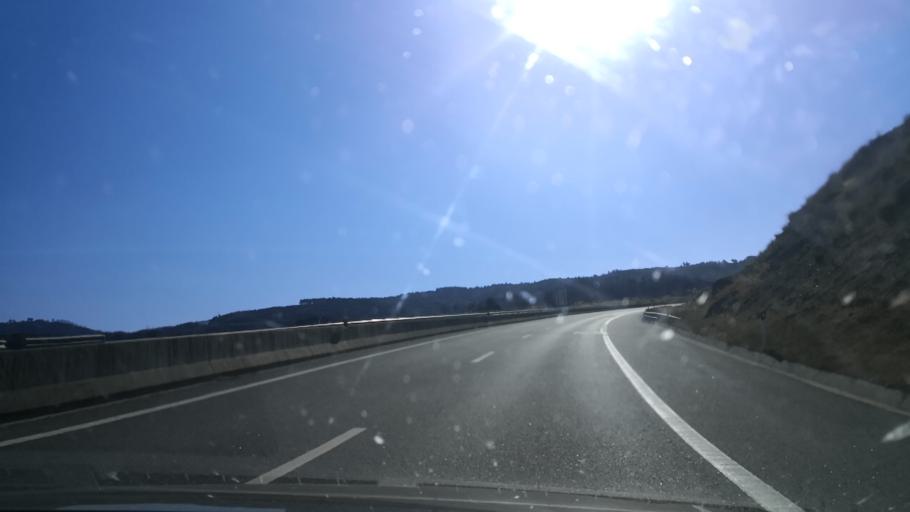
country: PT
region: Vila Real
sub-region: Murca
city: Murca
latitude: 41.3883
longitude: -7.4646
